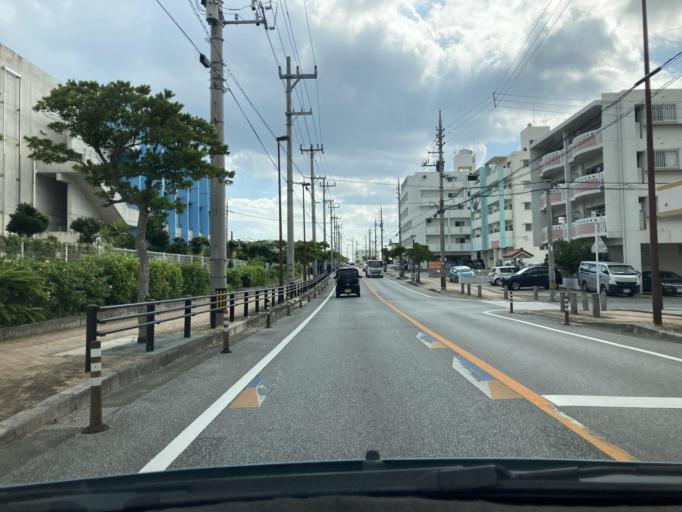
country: JP
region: Okinawa
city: Ginowan
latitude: 26.2484
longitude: 127.7732
